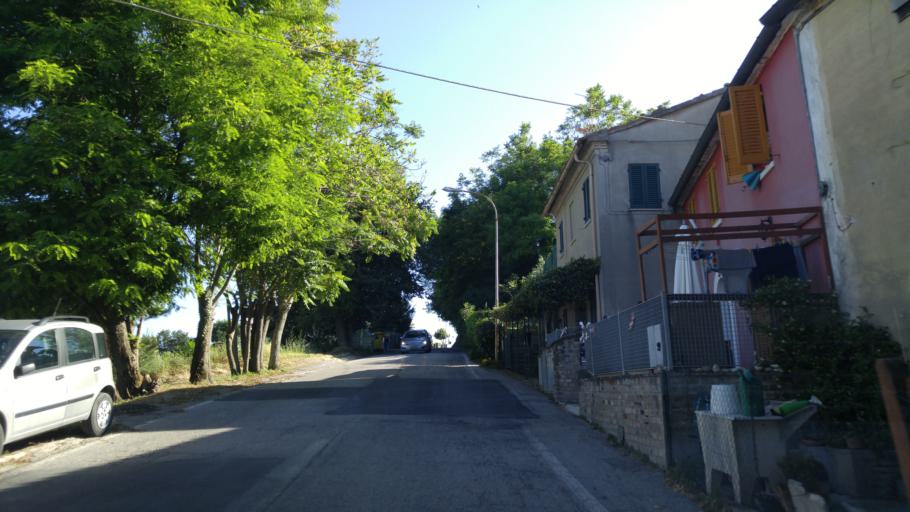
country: IT
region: The Marches
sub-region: Provincia di Pesaro e Urbino
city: Pesaro
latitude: 43.8590
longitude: 12.8944
